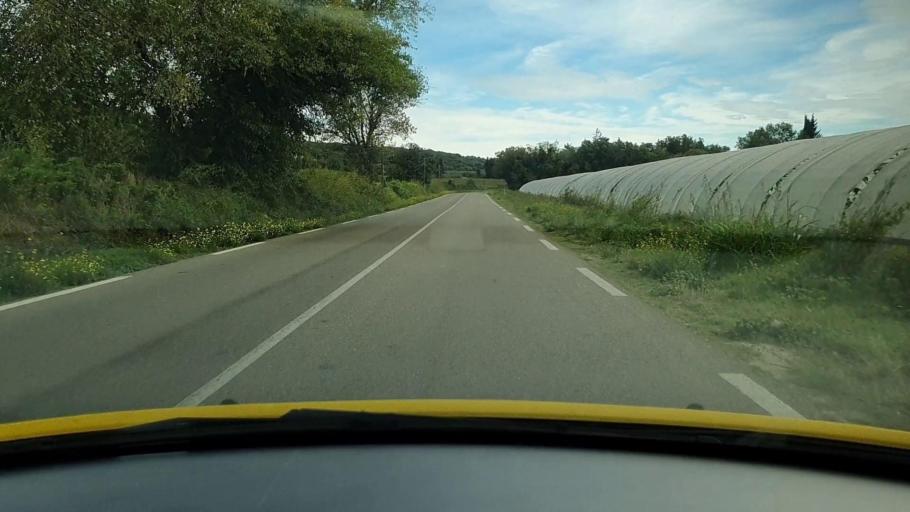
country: FR
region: Languedoc-Roussillon
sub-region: Departement du Gard
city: Bellegarde
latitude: 43.7687
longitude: 4.5328
